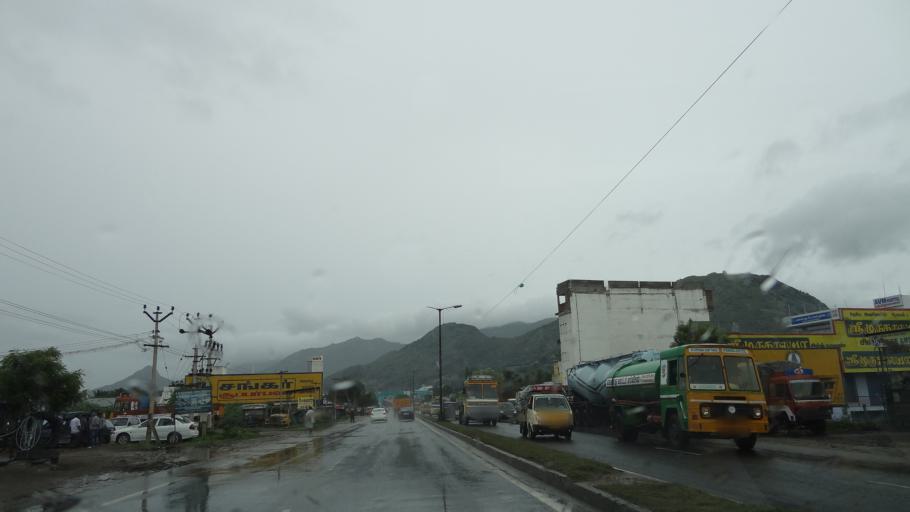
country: IN
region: Tamil Nadu
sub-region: Salem
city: Salem
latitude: 11.6272
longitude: 78.1391
